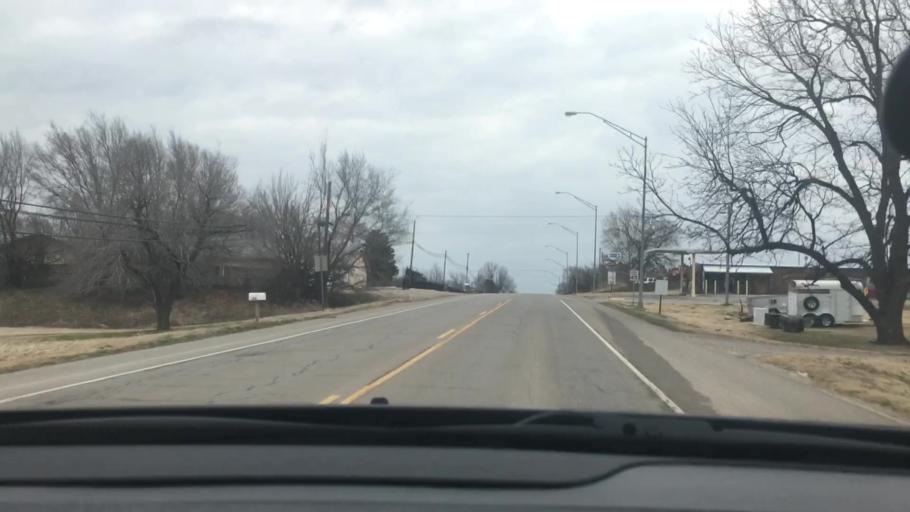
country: US
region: Oklahoma
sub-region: Garvin County
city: Maysville
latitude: 34.8175
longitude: -97.4217
